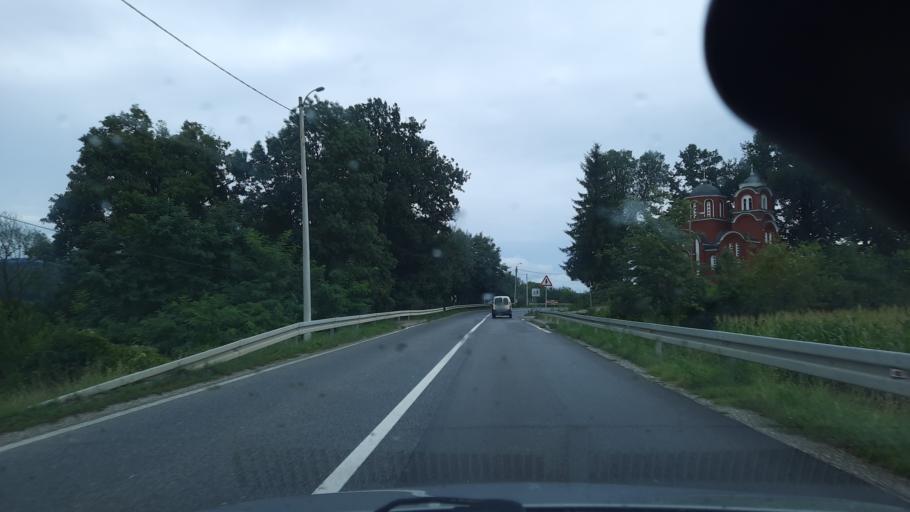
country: RS
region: Central Serbia
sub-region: Raski Okrug
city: Kraljevo
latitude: 43.7801
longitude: 20.7946
